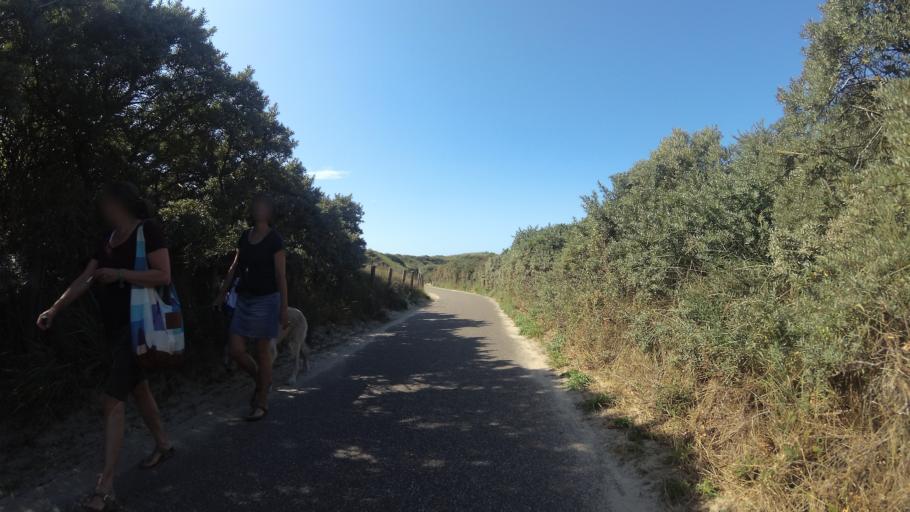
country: NL
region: Zeeland
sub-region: Gemeente Vlissingen
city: Vlissingen
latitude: 51.5155
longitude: 3.4521
